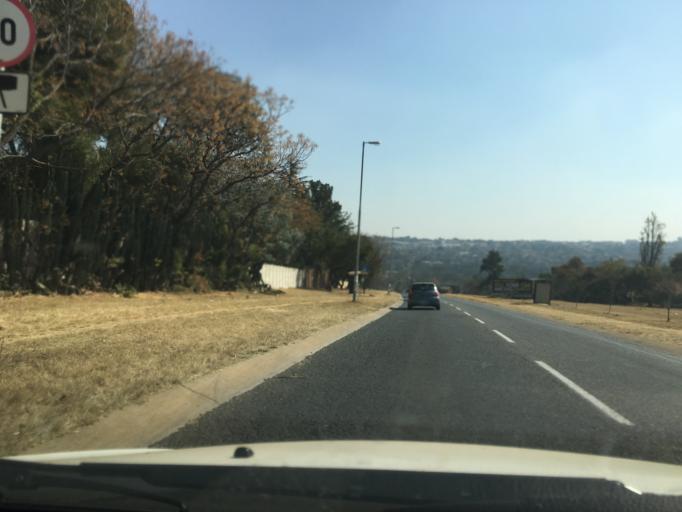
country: ZA
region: Gauteng
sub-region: City of Johannesburg Metropolitan Municipality
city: Midrand
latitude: -26.0746
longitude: 28.0443
